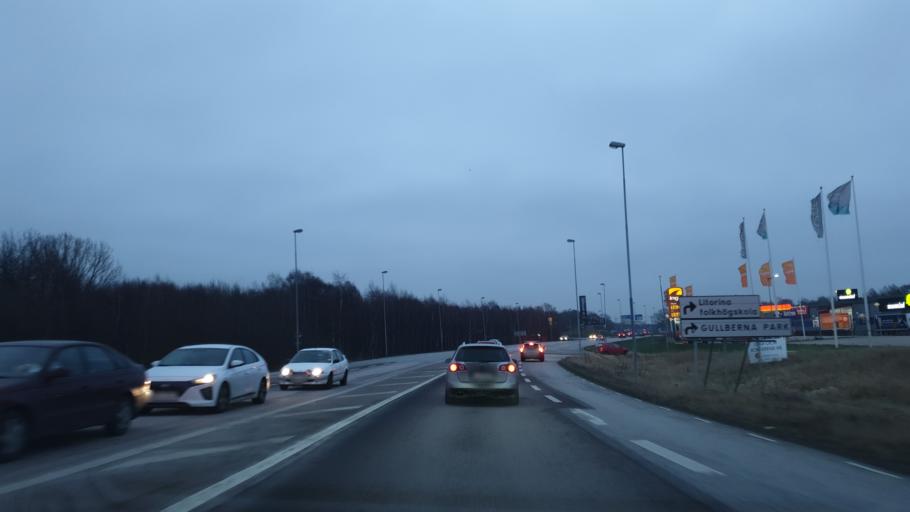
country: SE
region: Blekinge
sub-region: Karlskrona Kommun
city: Karlskrona
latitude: 56.1962
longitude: 15.6335
